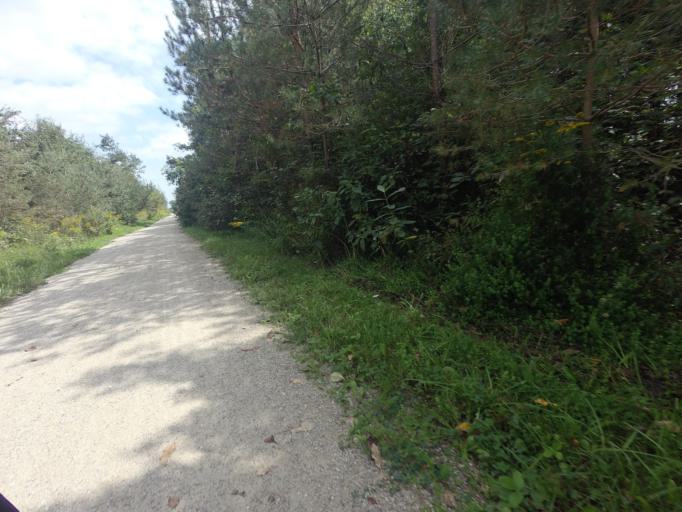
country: CA
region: Ontario
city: North Perth
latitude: 43.5743
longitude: -80.8334
